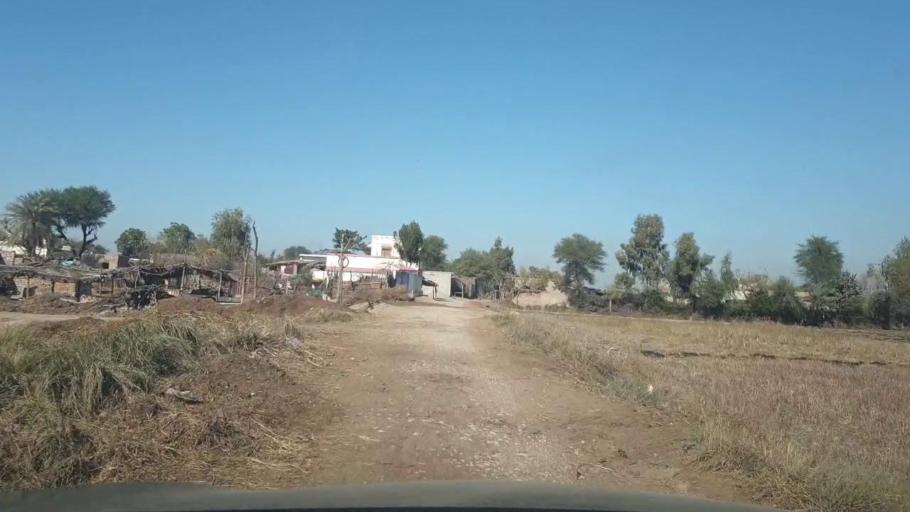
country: PK
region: Sindh
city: Mirpur Mathelo
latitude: 28.0807
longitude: 69.4893
